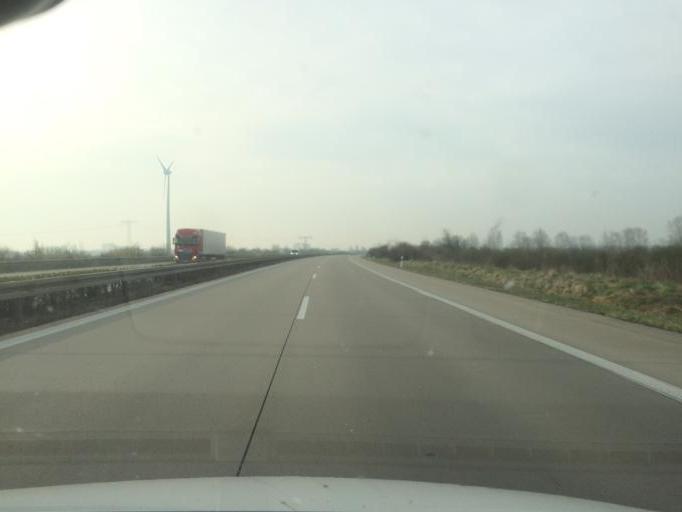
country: DE
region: Saxony-Anhalt
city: Geusa
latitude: 51.3296
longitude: 11.9364
